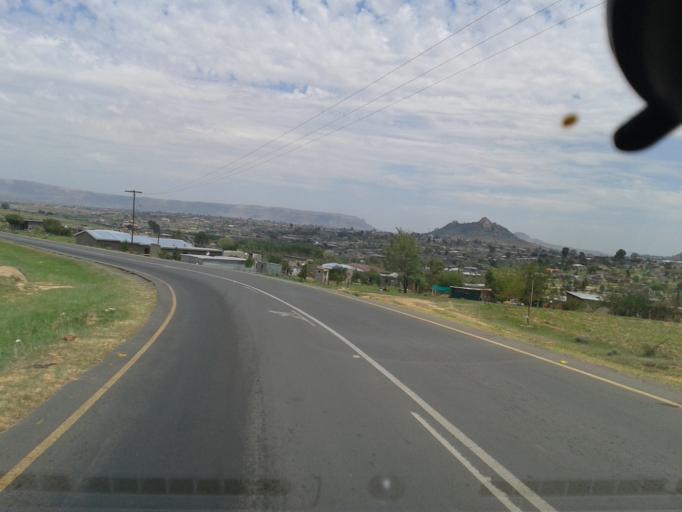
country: LS
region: Maseru
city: Maseru
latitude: -29.3549
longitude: 27.5727
